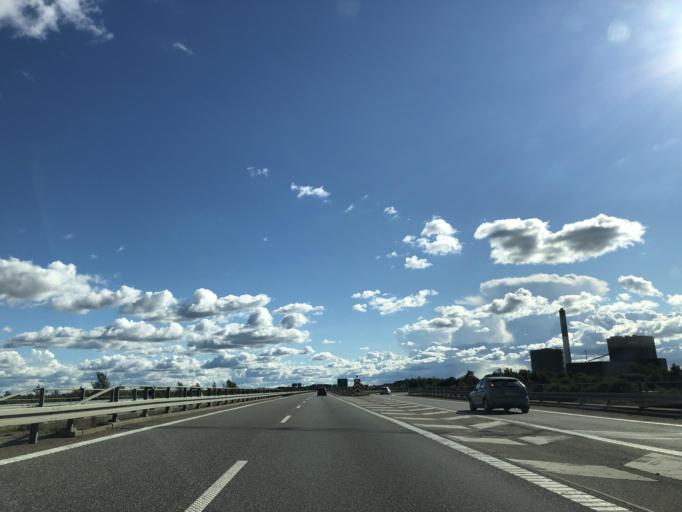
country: DK
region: Central Jutland
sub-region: Herning Kommune
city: Lind
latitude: 56.1275
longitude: 9.0113
